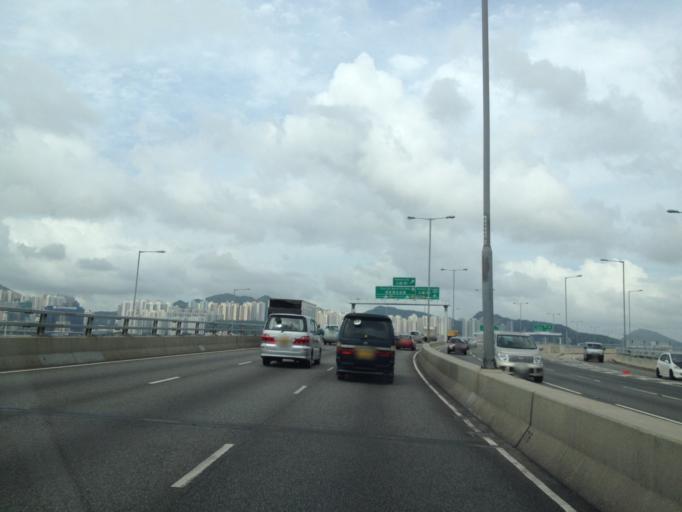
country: HK
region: Kowloon City
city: Kowloon
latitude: 22.2942
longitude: 114.2027
